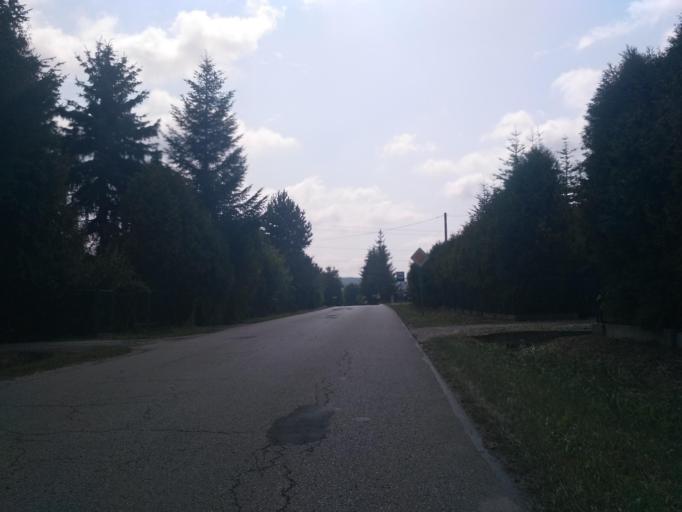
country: PL
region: Subcarpathian Voivodeship
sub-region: Powiat lancucki
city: Kraczkowa
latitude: 50.0301
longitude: 22.1895
